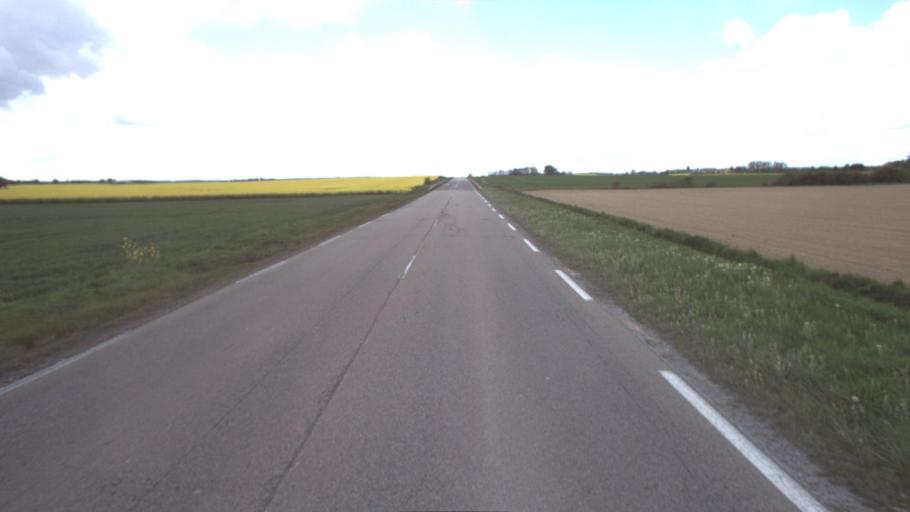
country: FR
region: Ile-de-France
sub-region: Departement de Seine-et-Marne
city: Villiers-Saint-Georges
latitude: 48.6919
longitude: 3.3737
